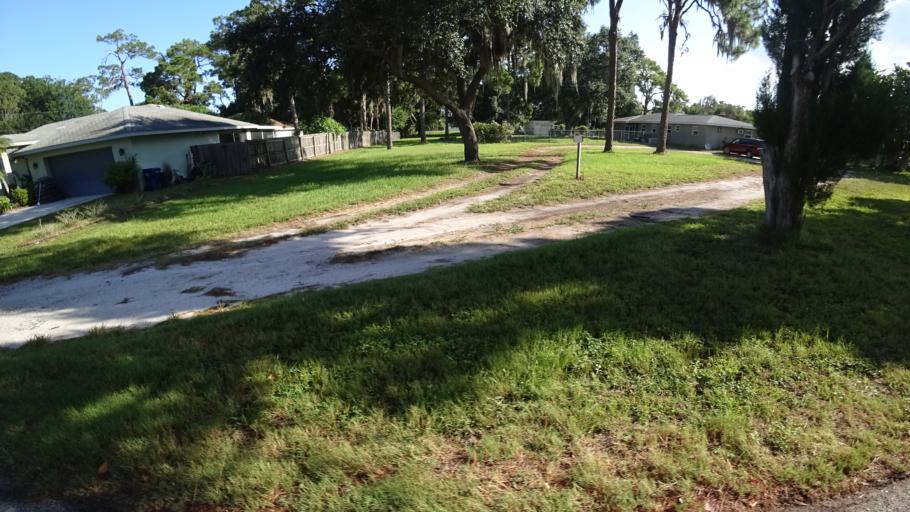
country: US
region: Florida
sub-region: Manatee County
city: South Bradenton
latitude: 27.4709
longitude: -82.5845
